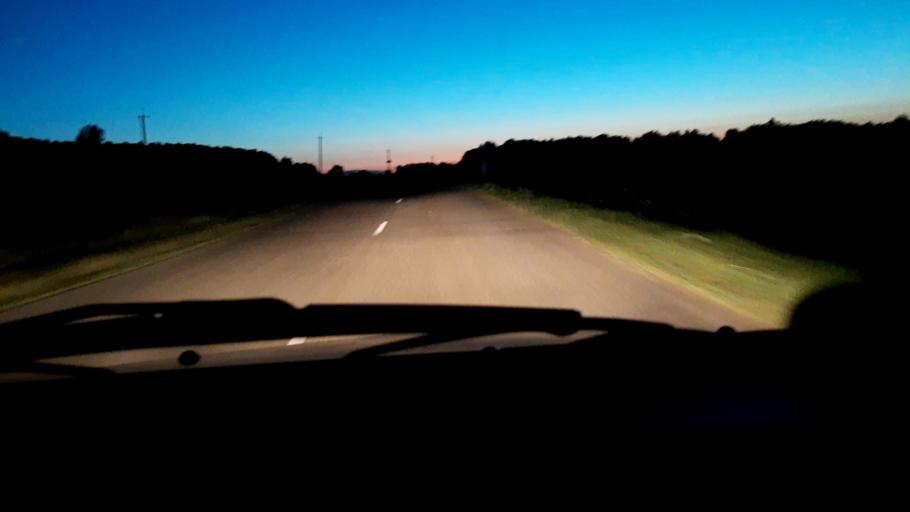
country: RU
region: Bashkortostan
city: Blagoveshchensk
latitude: 54.9374
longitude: 55.8926
